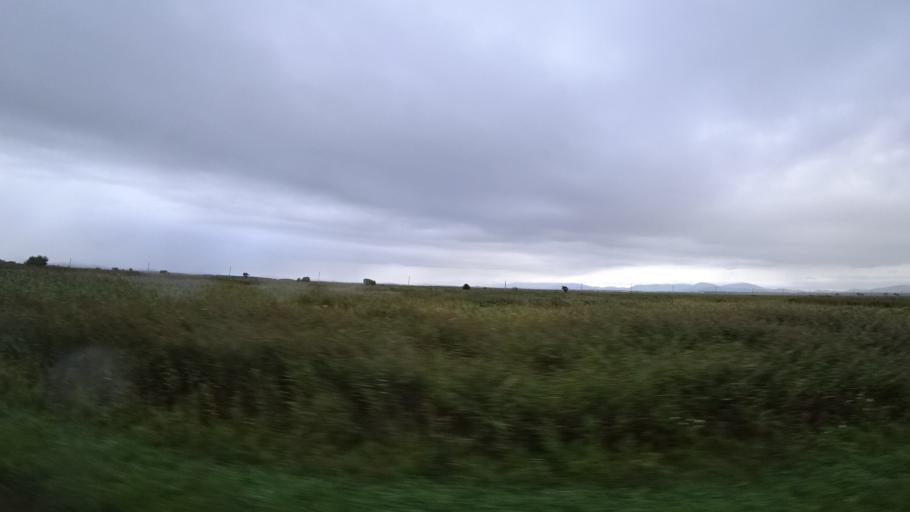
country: RU
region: Primorskiy
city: Chernigovka
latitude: 44.3888
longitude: 132.5294
